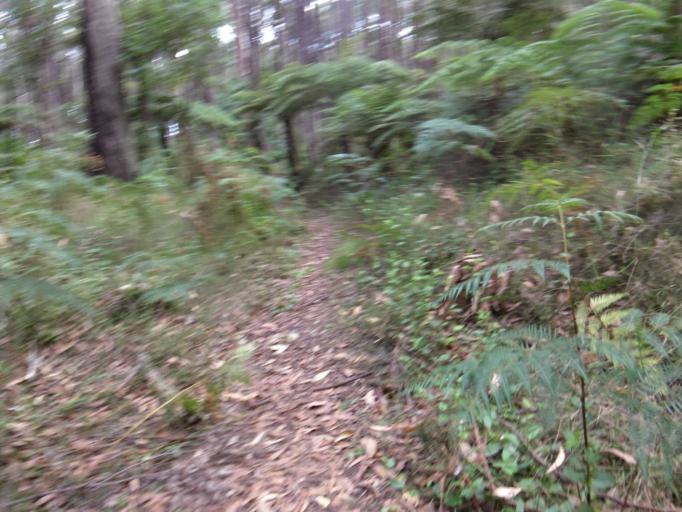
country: AU
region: Victoria
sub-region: Yarra Ranges
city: Healesville
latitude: -37.5418
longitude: 145.4783
